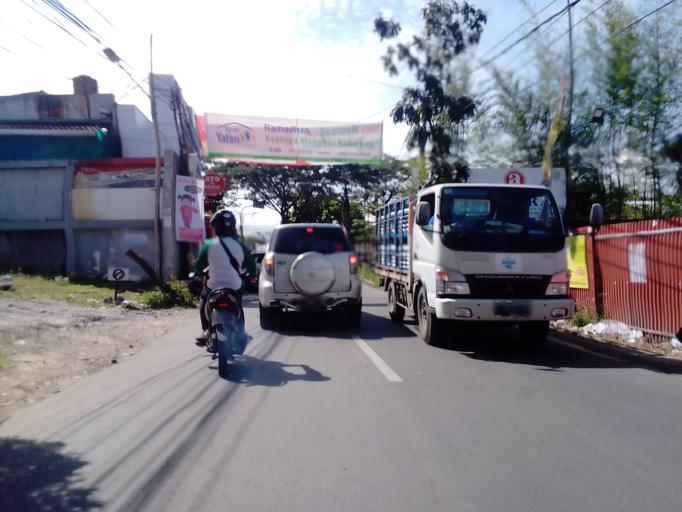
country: ID
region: West Java
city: Bandung
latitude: -6.9397
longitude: 107.6638
